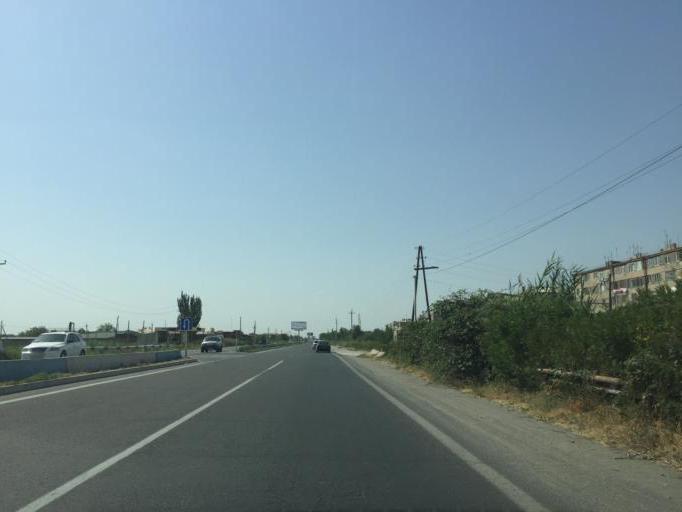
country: AM
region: Ararat
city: Artashat
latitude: 39.9461
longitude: 44.5489
